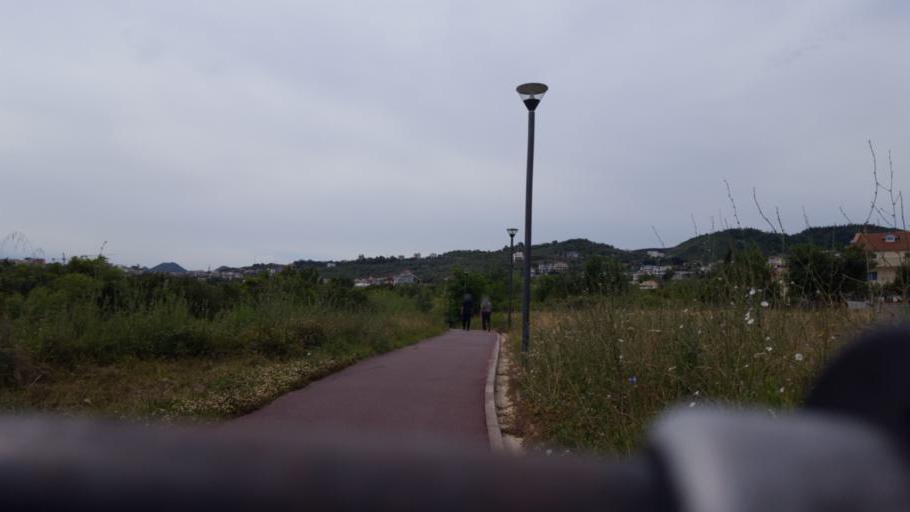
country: AL
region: Tirane
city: Tirana
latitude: 41.3077
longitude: 19.8198
